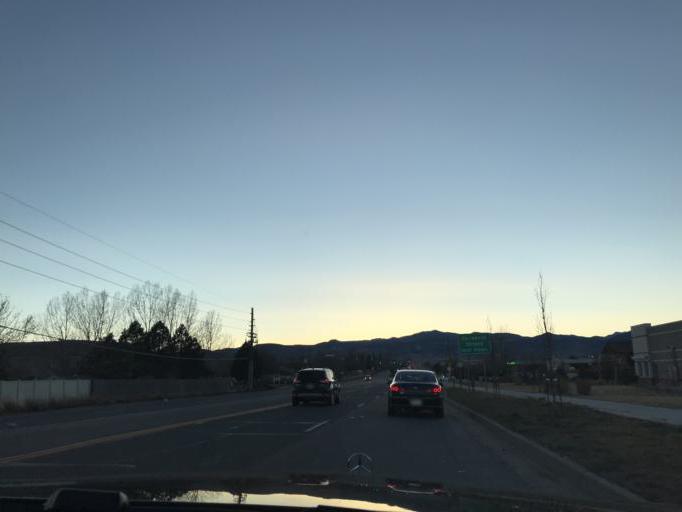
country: US
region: Colorado
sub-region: Jefferson County
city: Applewood
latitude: 39.8126
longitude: -105.1586
